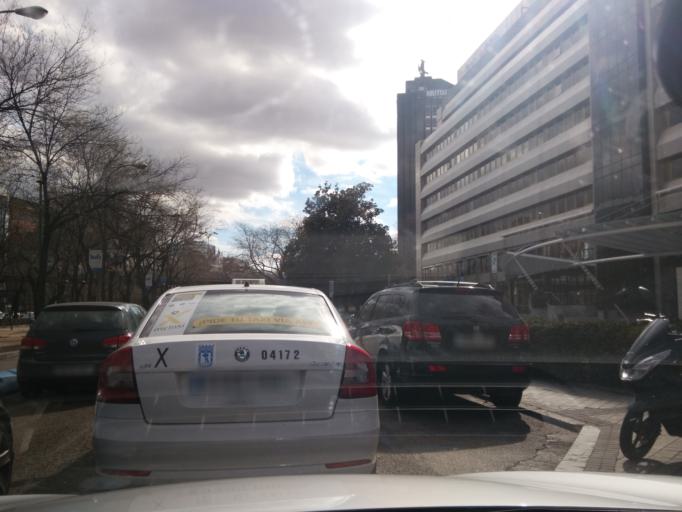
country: ES
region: Madrid
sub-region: Provincia de Madrid
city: Salamanca
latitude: 40.4341
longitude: -3.6890
